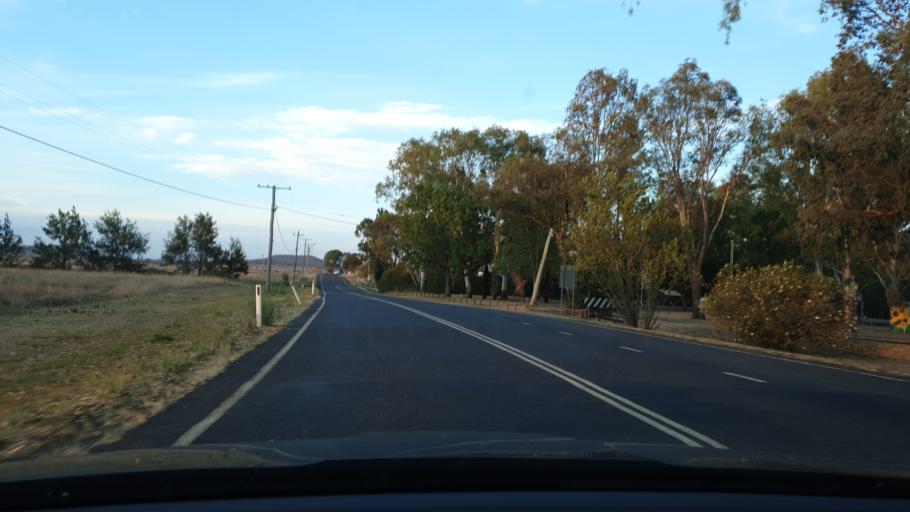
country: AU
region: Queensland
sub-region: Southern Downs
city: Warwick
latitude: -28.0293
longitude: 151.9826
